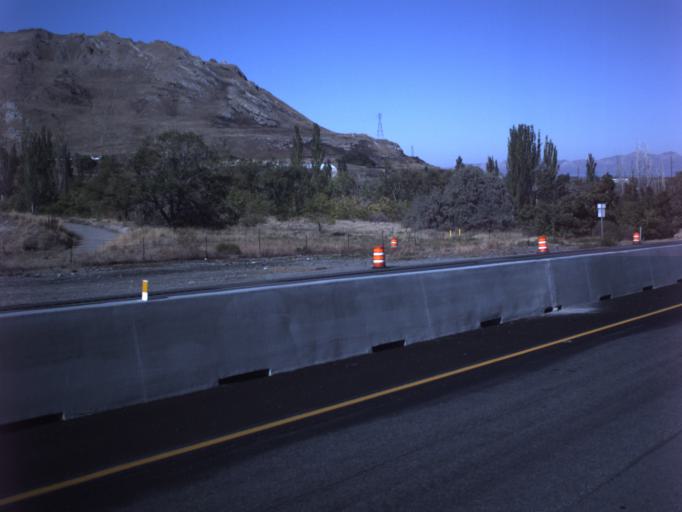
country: US
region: Utah
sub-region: Salt Lake County
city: Magna
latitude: 40.7248
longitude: -112.1605
